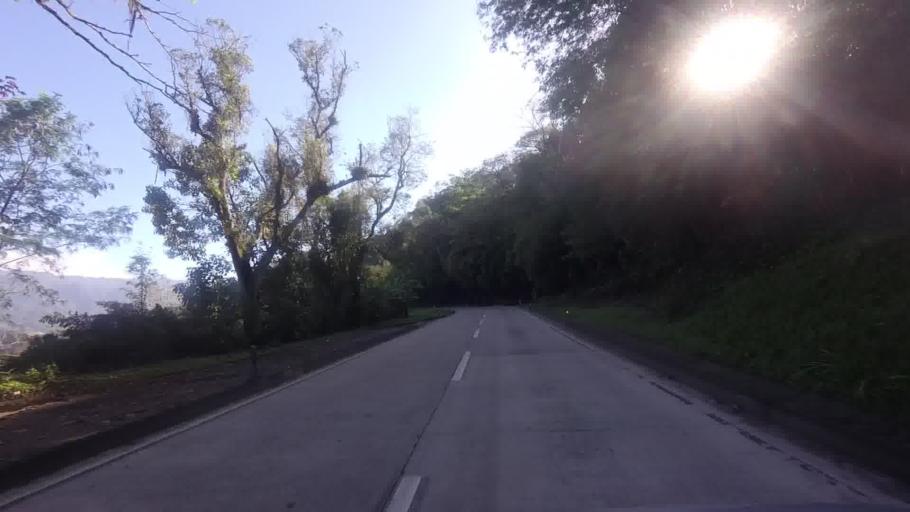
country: BR
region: Rio de Janeiro
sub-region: Petropolis
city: Petropolis
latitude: -22.5791
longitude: -43.2628
